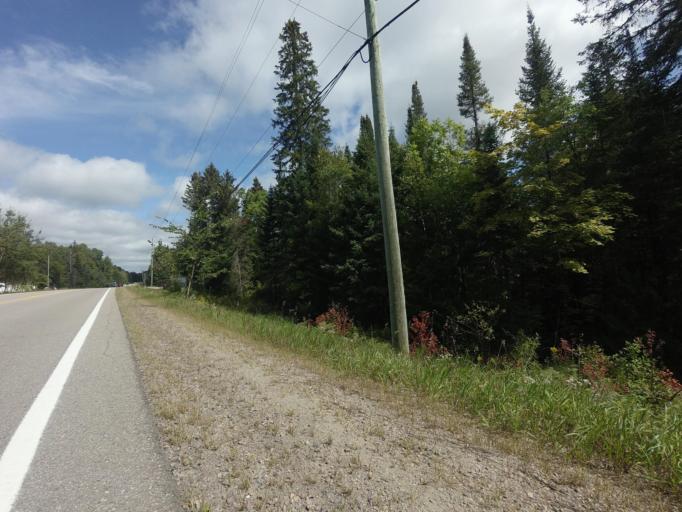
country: CA
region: Ontario
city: Omemee
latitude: 44.8328
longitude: -78.5589
